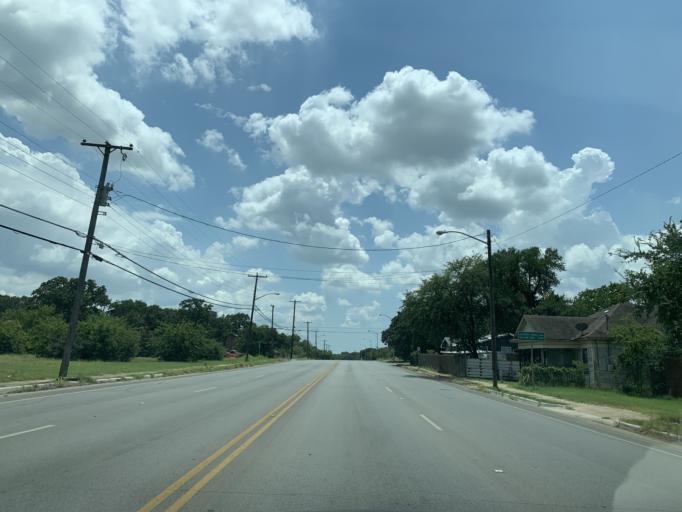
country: US
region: Texas
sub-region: Tarrant County
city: Forest Hill
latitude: 32.7280
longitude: -97.2620
